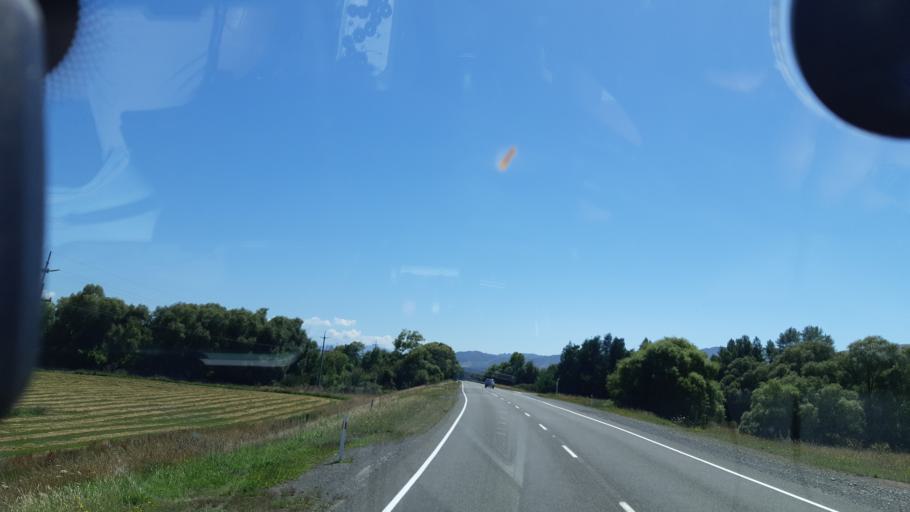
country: NZ
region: Canterbury
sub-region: Kaikoura District
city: Kaikoura
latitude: -42.7262
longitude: 173.2800
